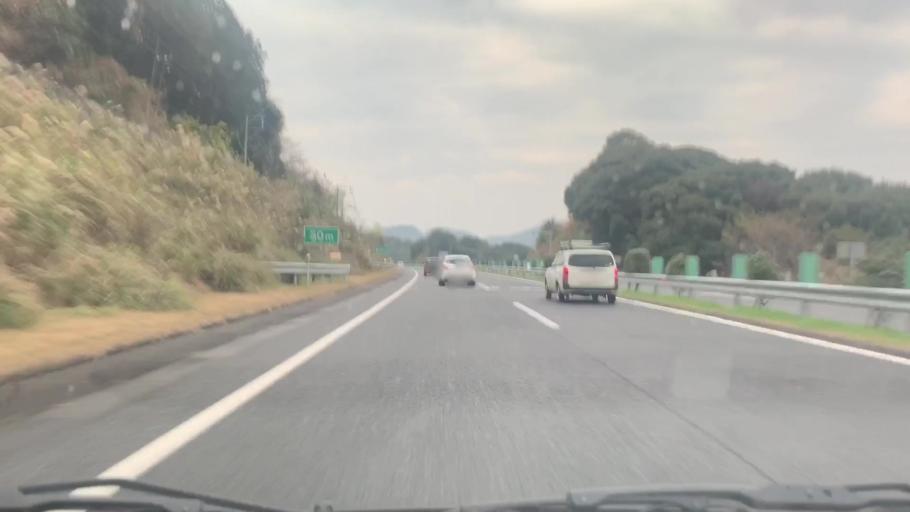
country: JP
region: Nagasaki
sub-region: Isahaya-shi
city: Isahaya
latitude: 32.8217
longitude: 129.9869
